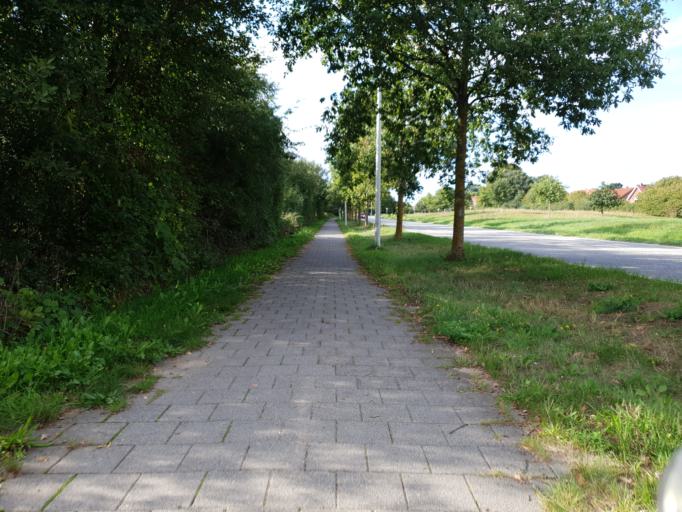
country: DE
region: Schleswig-Holstein
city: Kronshagen
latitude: 54.3493
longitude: 10.0735
